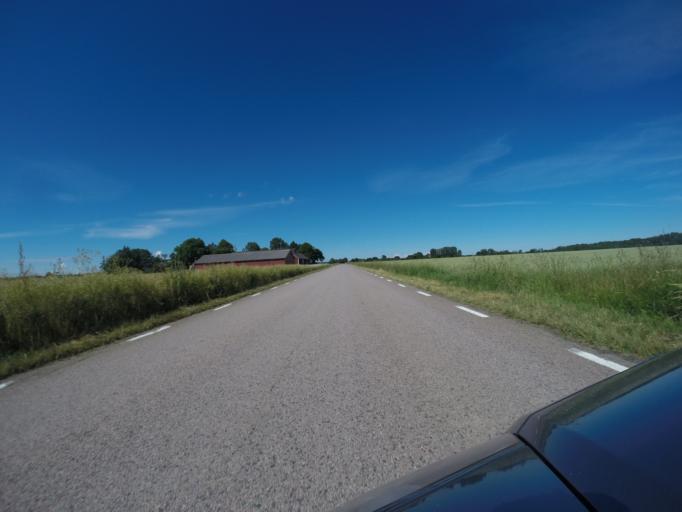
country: SE
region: Skane
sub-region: Helsingborg
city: Odakra
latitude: 56.1385
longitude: 12.7531
